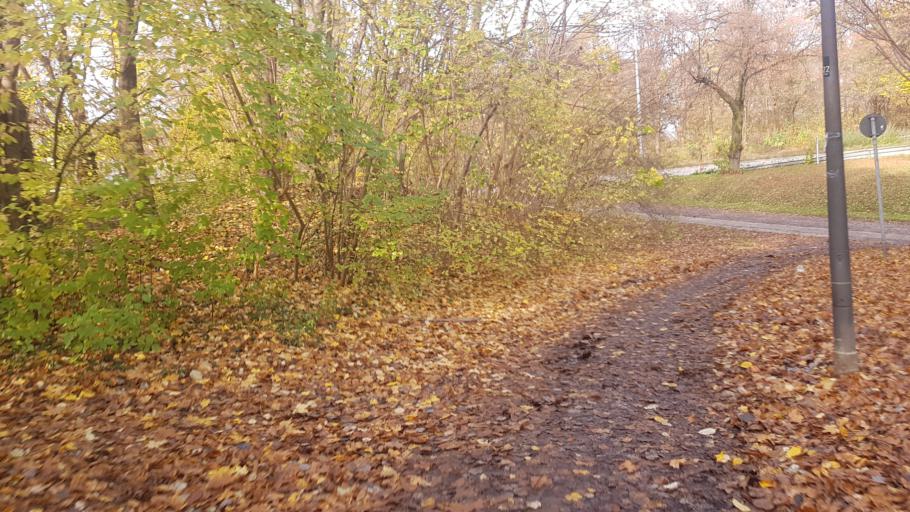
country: DE
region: Bavaria
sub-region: Upper Bavaria
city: Unterhaching
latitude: 48.1049
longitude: 11.6100
